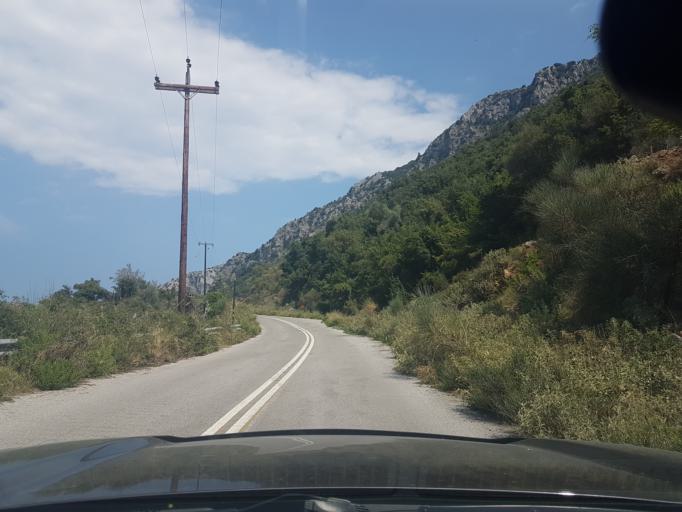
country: GR
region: Central Greece
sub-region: Nomos Evvoias
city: Kymi
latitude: 38.6416
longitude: 23.9592
